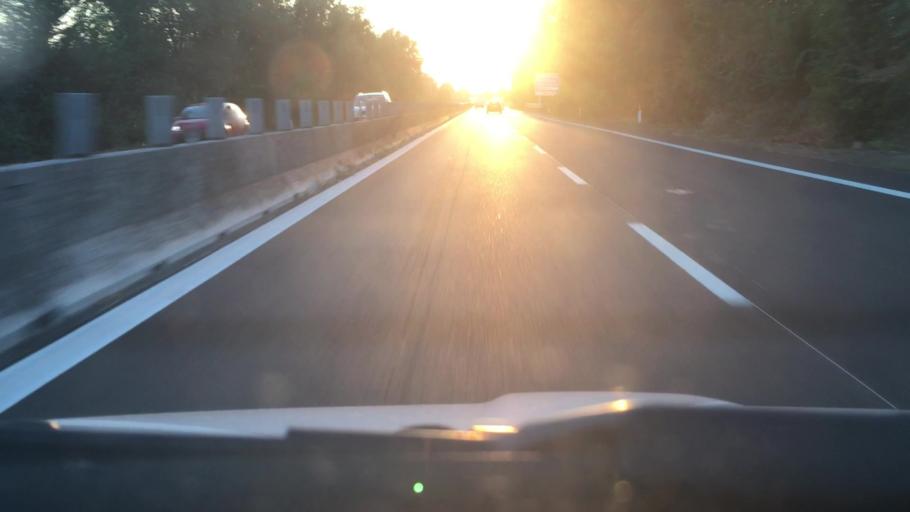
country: IT
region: Emilia-Romagna
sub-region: Provincia di Ferrara
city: Cona
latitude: 44.7908
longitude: 11.7115
